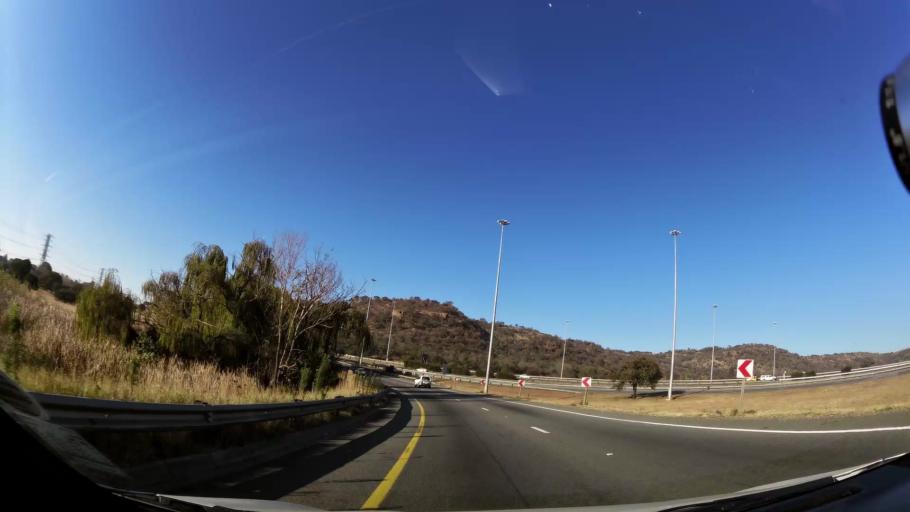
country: ZA
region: Gauteng
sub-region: City of Johannesburg Metropolitan Municipality
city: Johannesburg
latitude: -26.2661
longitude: 28.0971
